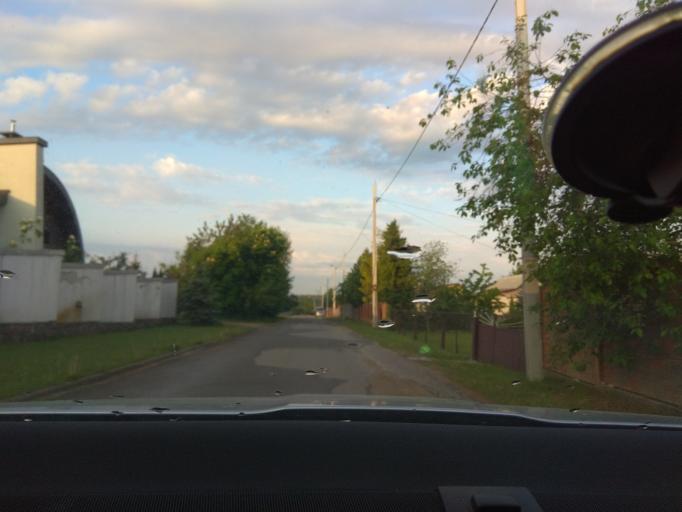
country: BY
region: Grodnenskaya
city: Hrodna
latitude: 53.6467
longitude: 23.7854
